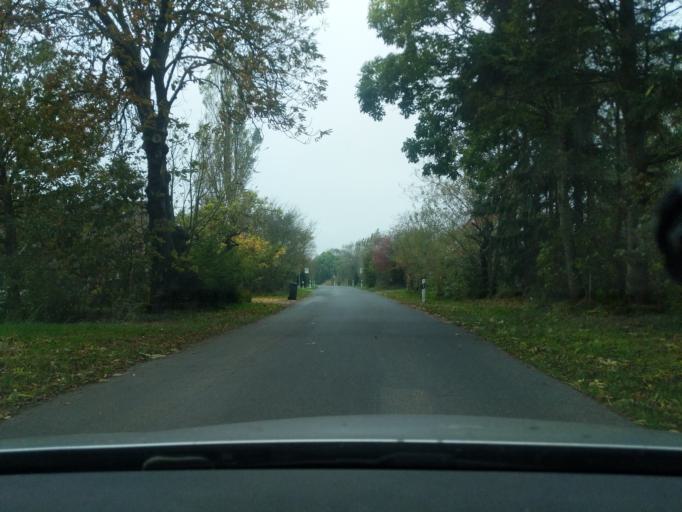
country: DE
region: Lower Saxony
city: Nordleda
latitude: 53.8281
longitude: 8.8110
